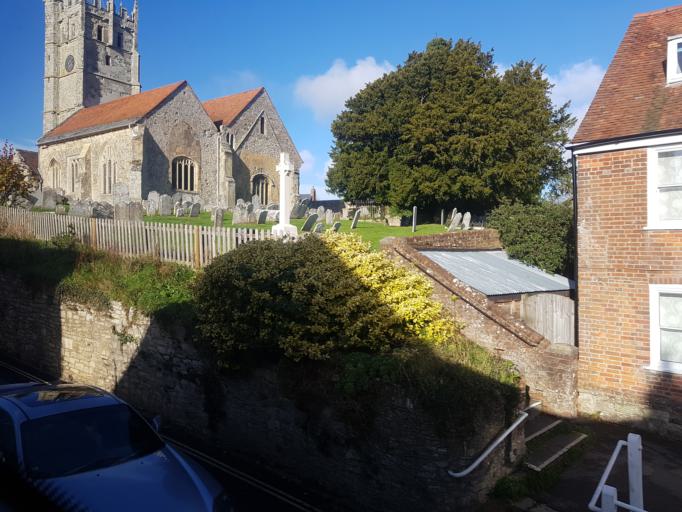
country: GB
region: England
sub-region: Isle of Wight
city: Newport
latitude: 50.6916
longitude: -1.3131
